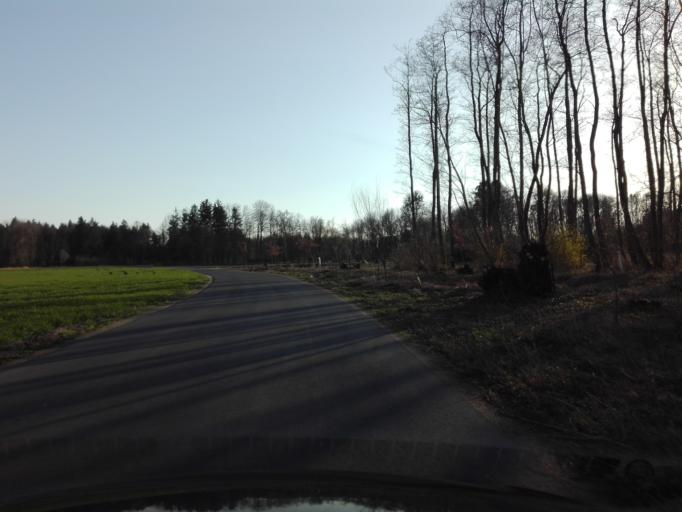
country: AT
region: Upper Austria
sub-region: Politischer Bezirk Perg
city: Perg
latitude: 48.2149
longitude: 14.6942
